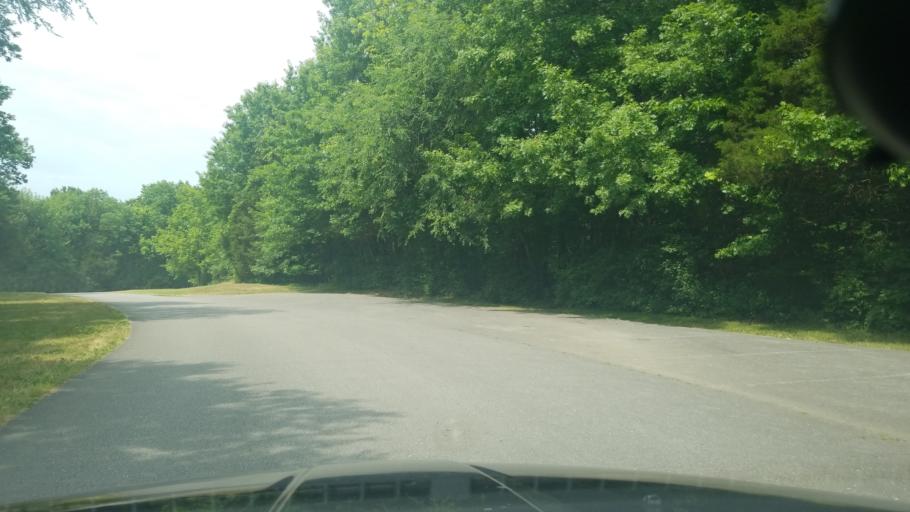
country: US
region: Tennessee
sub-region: Davidson County
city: Goodlettsville
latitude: 36.2710
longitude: -86.7494
